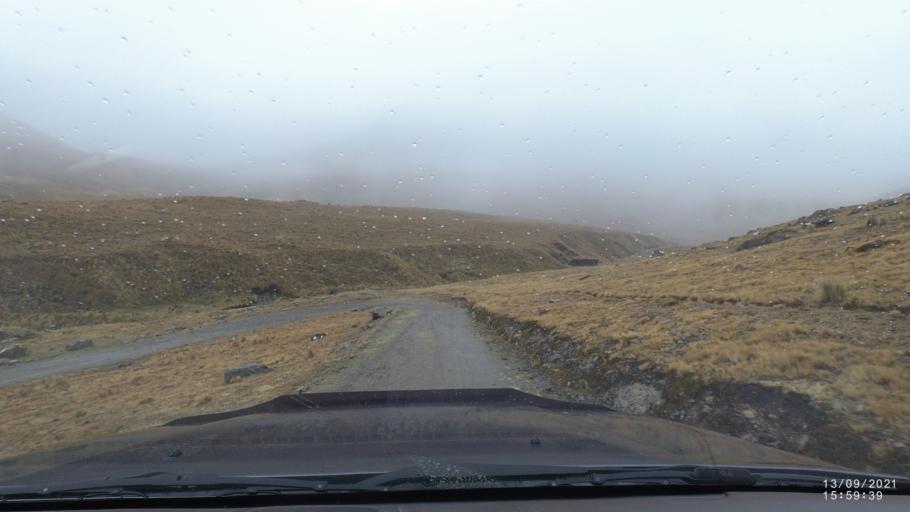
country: BO
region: Cochabamba
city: Colomi
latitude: -17.2966
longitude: -65.7075
